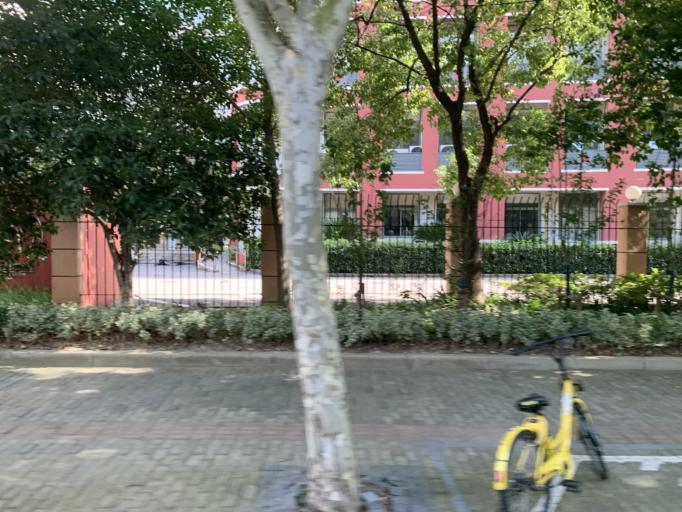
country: CN
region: Shanghai Shi
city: Huamu
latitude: 31.2165
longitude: 121.5287
